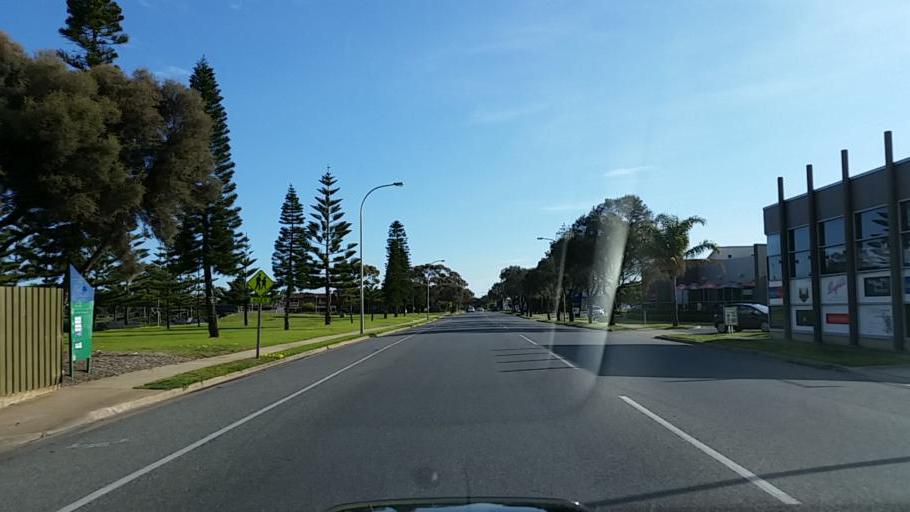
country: AU
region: South Australia
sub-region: Charles Sturt
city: West Lakes Shore
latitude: -34.8596
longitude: 138.4919
